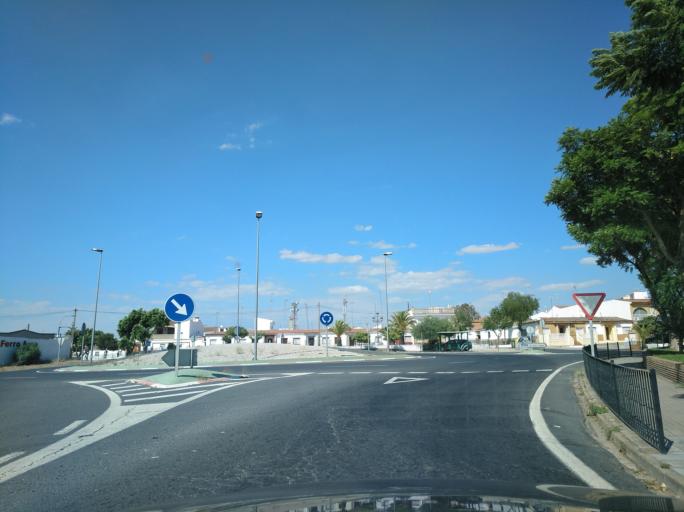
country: ES
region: Andalusia
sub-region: Provincia de Huelva
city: Alosno
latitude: 37.5490
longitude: -7.1201
